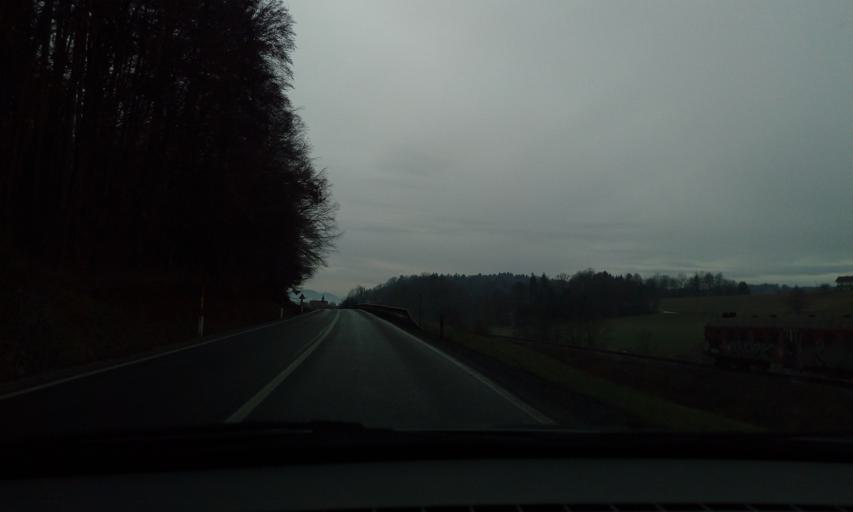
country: SI
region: Smarje pri Jelsah
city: Smarje pri Jelsah
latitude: 46.2293
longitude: 15.4774
